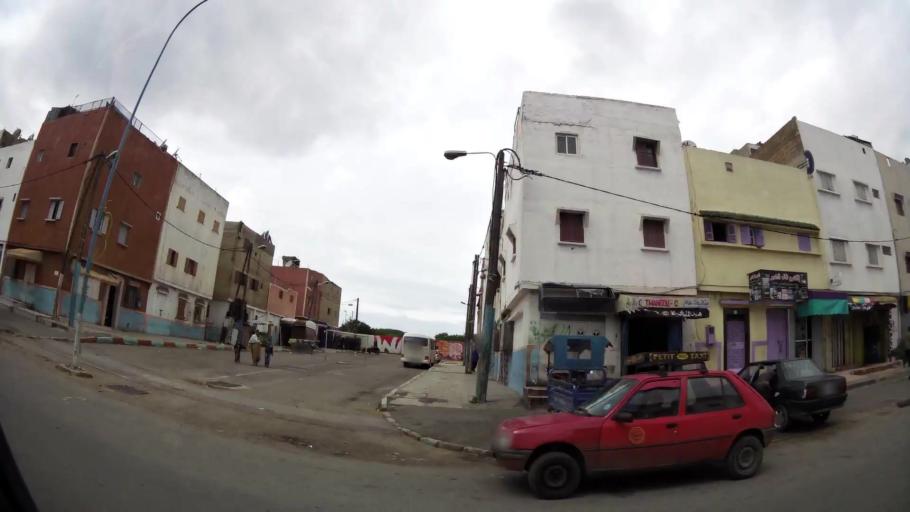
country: MA
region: Grand Casablanca
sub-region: Casablanca
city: Casablanca
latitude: 33.5757
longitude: -7.5698
